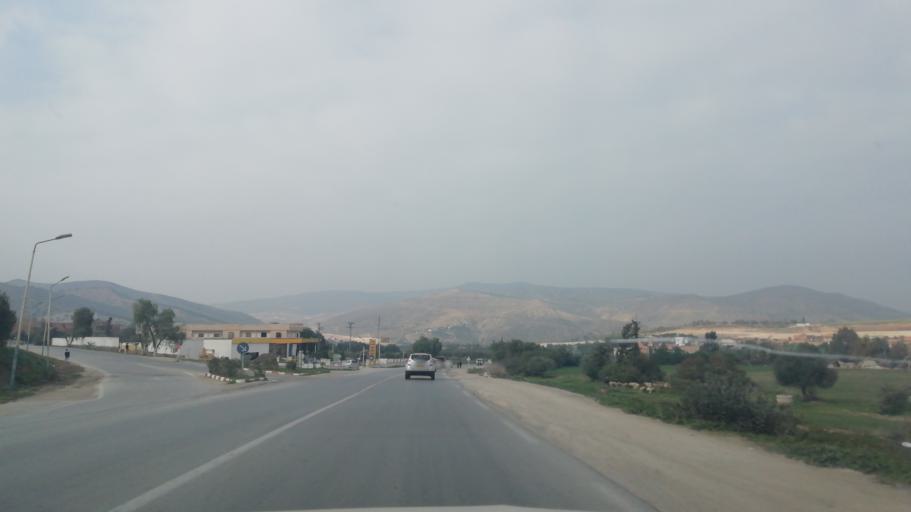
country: DZ
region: Mascara
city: Mascara
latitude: 35.4575
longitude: 0.0024
